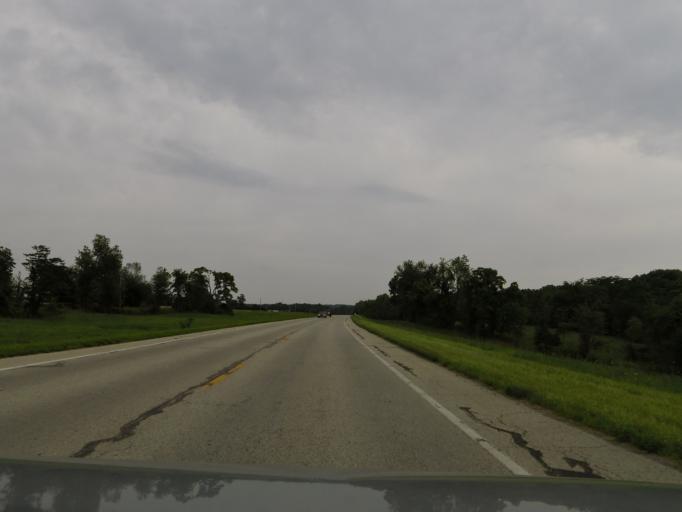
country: US
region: Ohio
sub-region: Brown County
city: Georgetown
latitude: 38.8491
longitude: -83.8488
